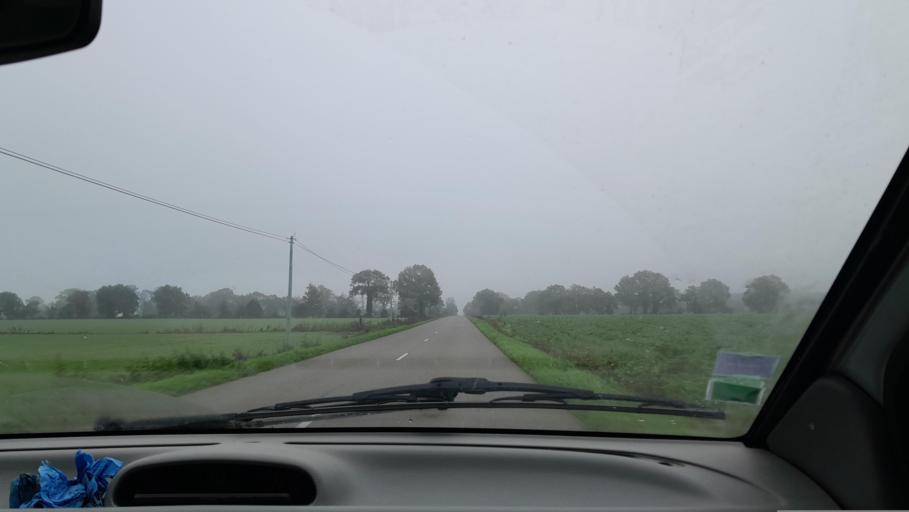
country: FR
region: Brittany
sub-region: Departement d'Ille-et-Vilaine
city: Le Pertre
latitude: 47.9718
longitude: -1.0304
